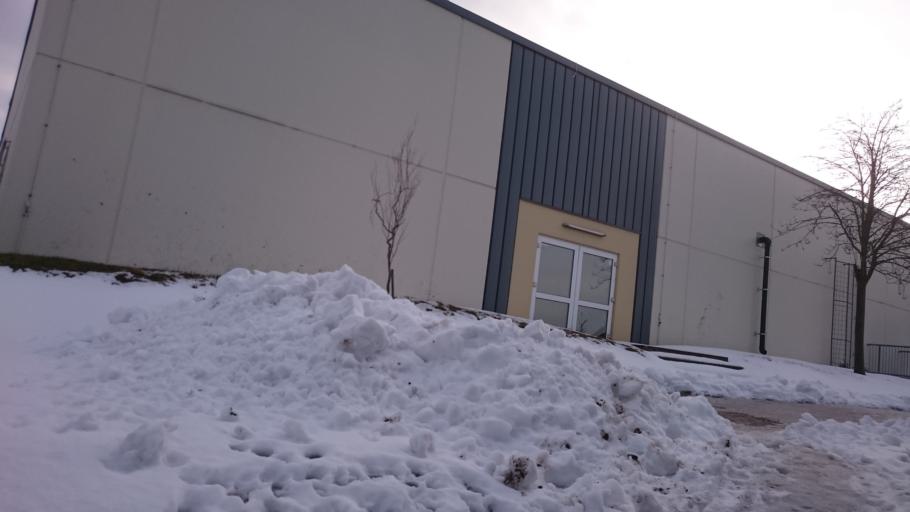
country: DE
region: Saxony
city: Zwickau
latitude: 50.7203
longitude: 12.5231
